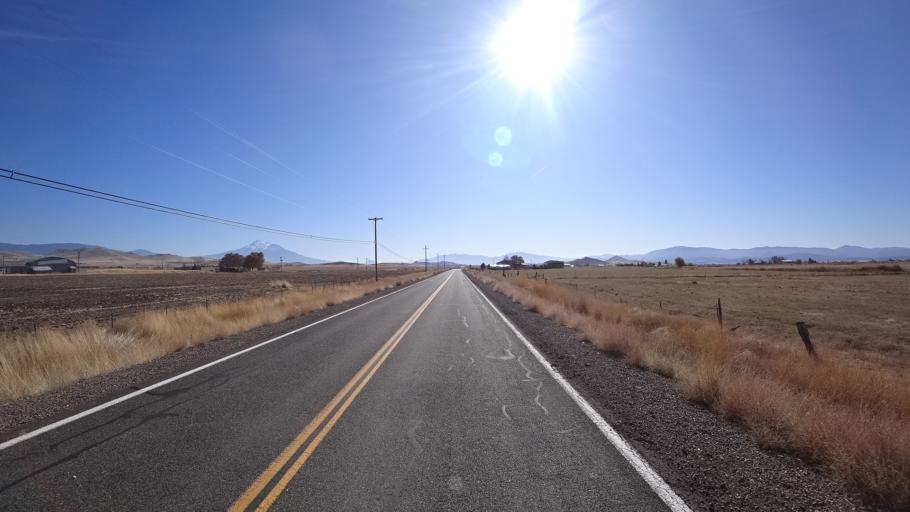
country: US
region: California
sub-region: Siskiyou County
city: Montague
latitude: 41.7804
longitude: -122.4737
